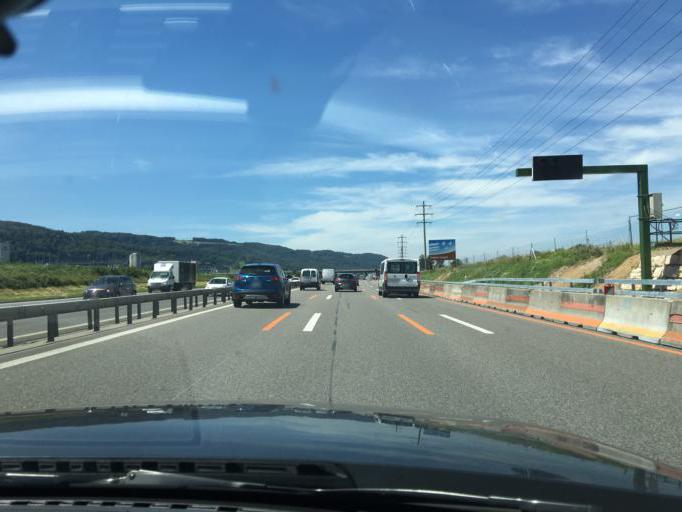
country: CH
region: Zurich
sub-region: Bezirk Dietikon
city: Dietikon / Vorstadt
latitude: 47.4237
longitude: 8.3839
